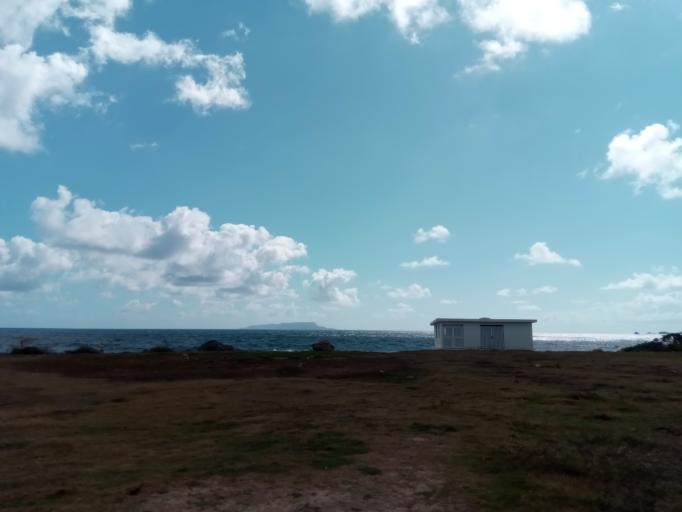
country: GP
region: Guadeloupe
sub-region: Guadeloupe
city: Saint-Francois
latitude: 16.2779
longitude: -61.2466
